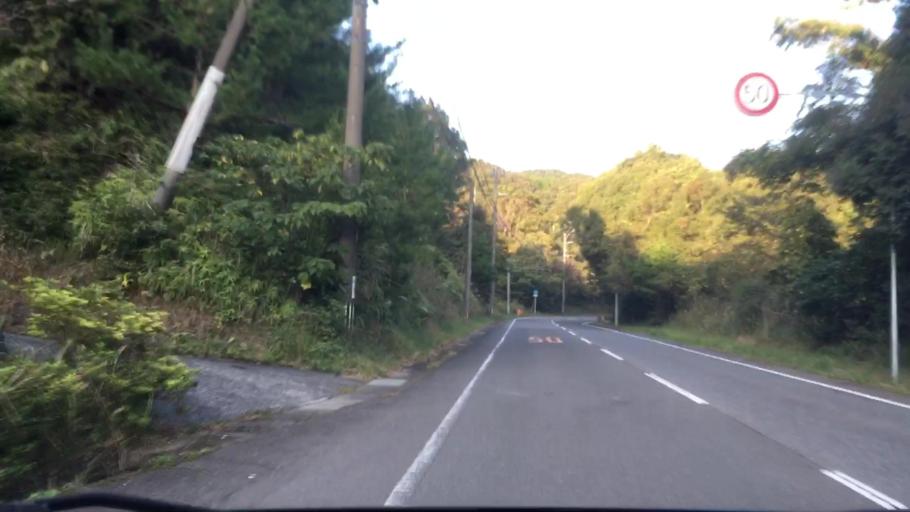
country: JP
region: Nagasaki
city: Sasebo
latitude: 32.9748
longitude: 129.7042
